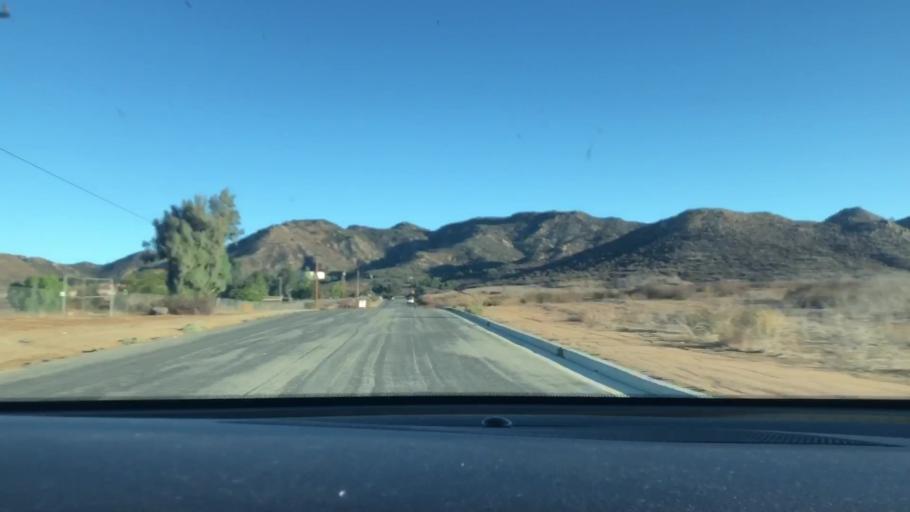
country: US
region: California
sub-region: Riverside County
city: Wildomar
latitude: 33.6006
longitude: -117.2324
